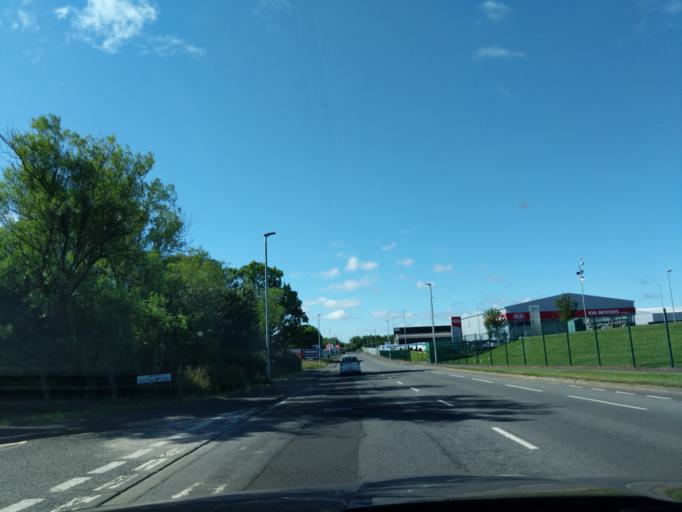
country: GB
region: England
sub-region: Northumberland
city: Ashington
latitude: 55.1685
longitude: -1.5492
